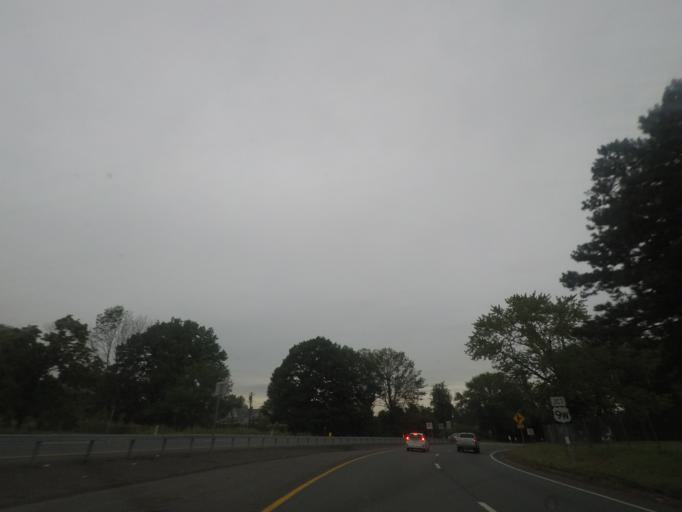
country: US
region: New York
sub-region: Albany County
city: Albany
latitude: 42.6342
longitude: -73.7775
